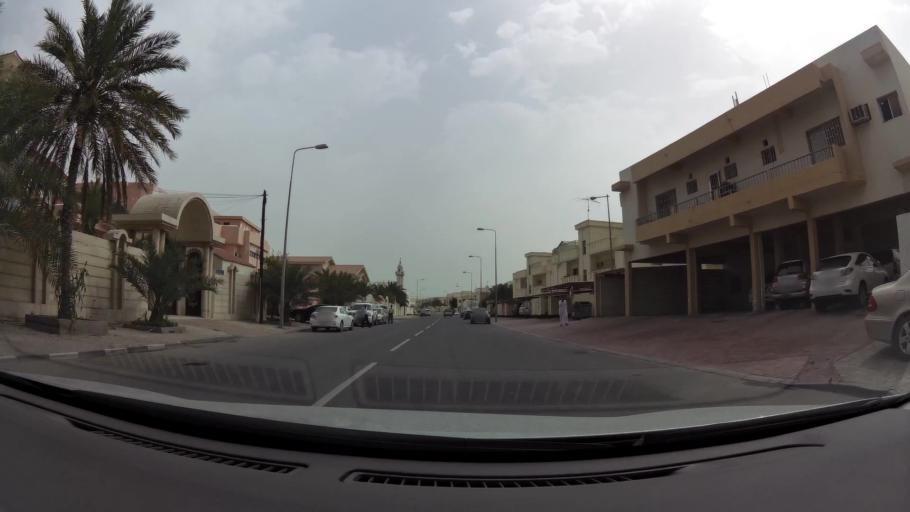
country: QA
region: Baladiyat ad Dawhah
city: Doha
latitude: 25.2602
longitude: 51.5474
